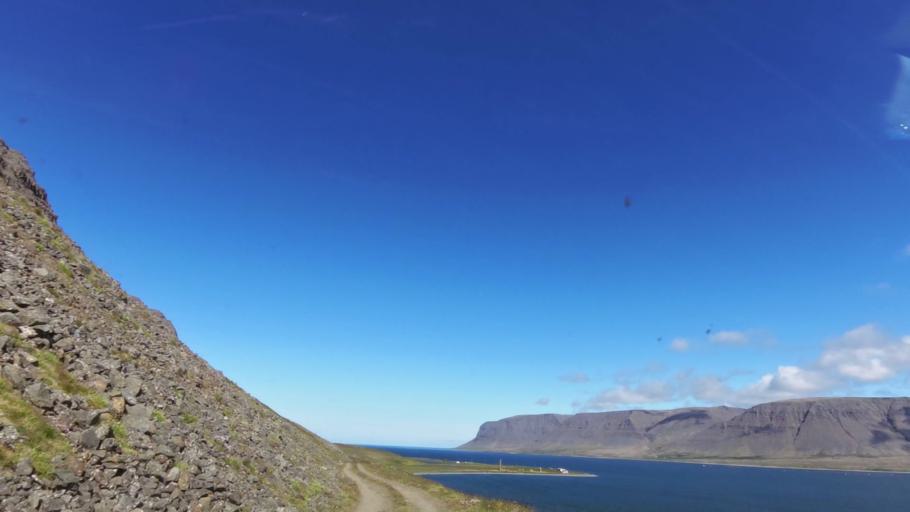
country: IS
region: West
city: Olafsvik
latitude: 65.6332
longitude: -23.9209
